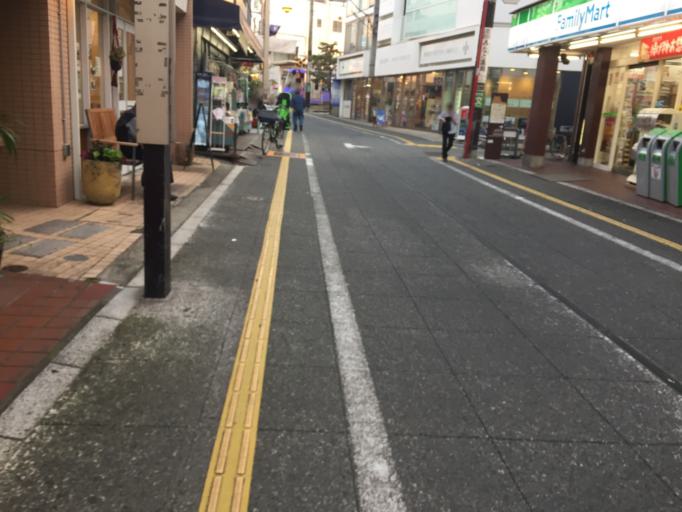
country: JP
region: Tokyo
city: Tokyo
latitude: 35.6445
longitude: 139.6555
